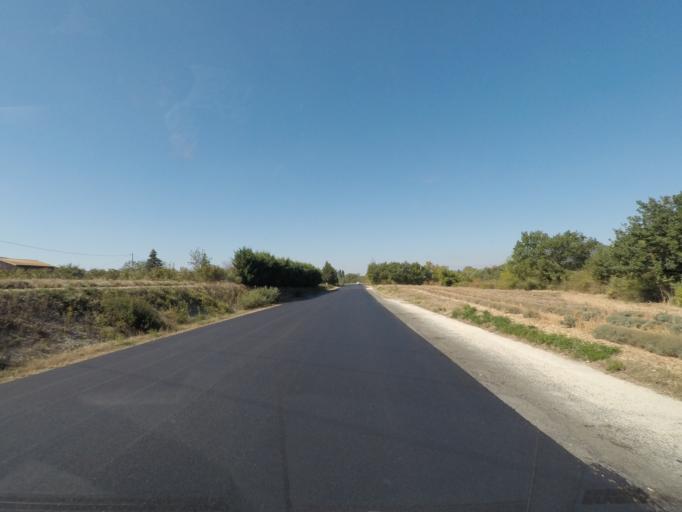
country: FR
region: Rhone-Alpes
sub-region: Departement de la Drome
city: Aouste-sur-Sye
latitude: 44.7040
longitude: 5.1039
